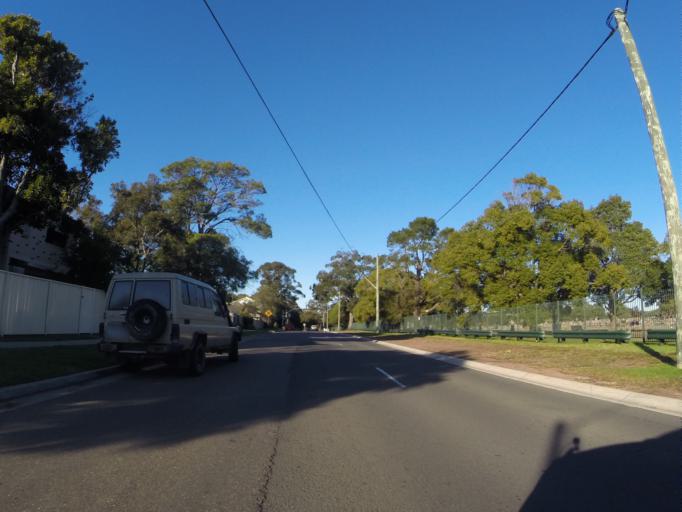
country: AU
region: New South Wales
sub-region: Sutherland Shire
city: Loftus
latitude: -34.0337
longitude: 151.0543
